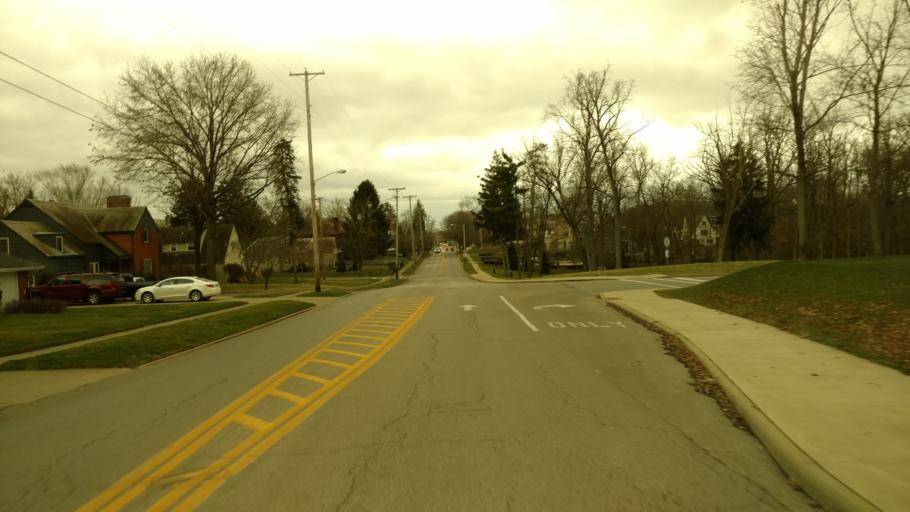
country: US
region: Ohio
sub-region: Muskingum County
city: Zanesville
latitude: 39.9578
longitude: -82.0168
